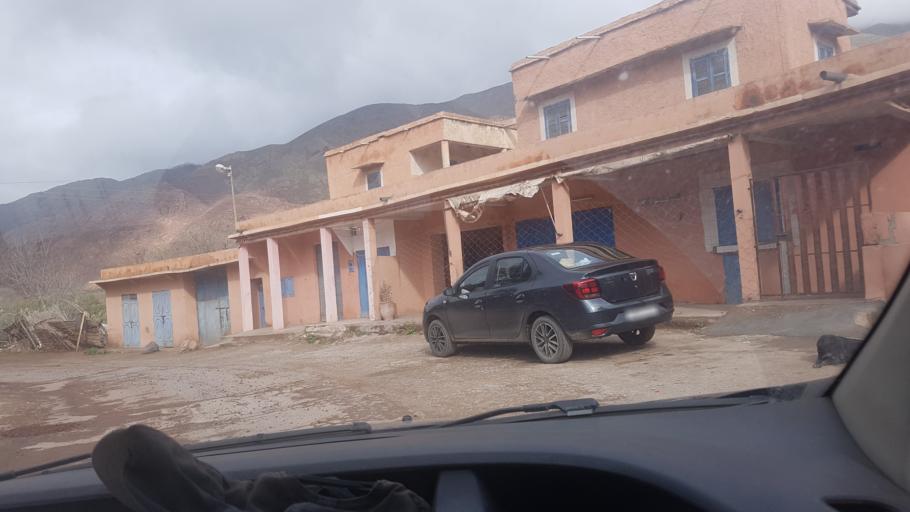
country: MA
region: Marrakech-Tensift-Al Haouz
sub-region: Al-Haouz
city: Azgour
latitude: 30.9998
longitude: -8.1583
